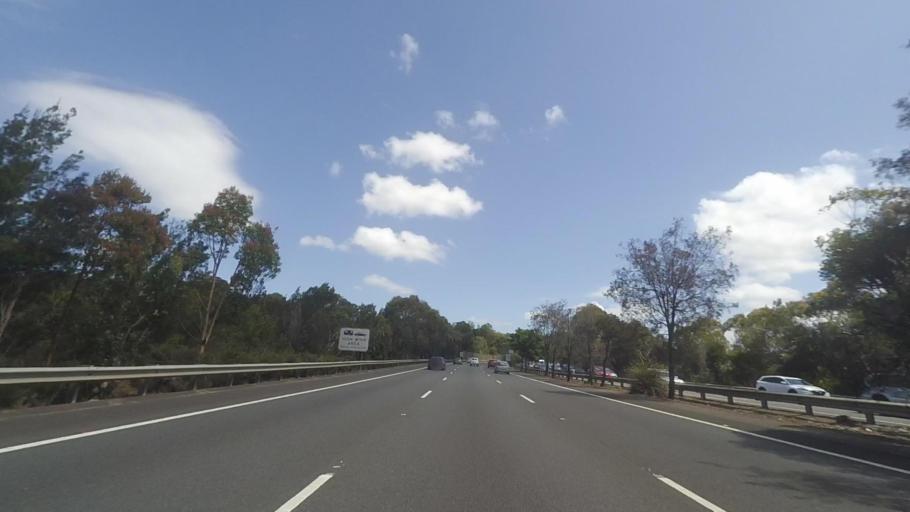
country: AU
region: New South Wales
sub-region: Hornsby Shire
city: Mount Colah
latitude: -33.6918
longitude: 151.1216
